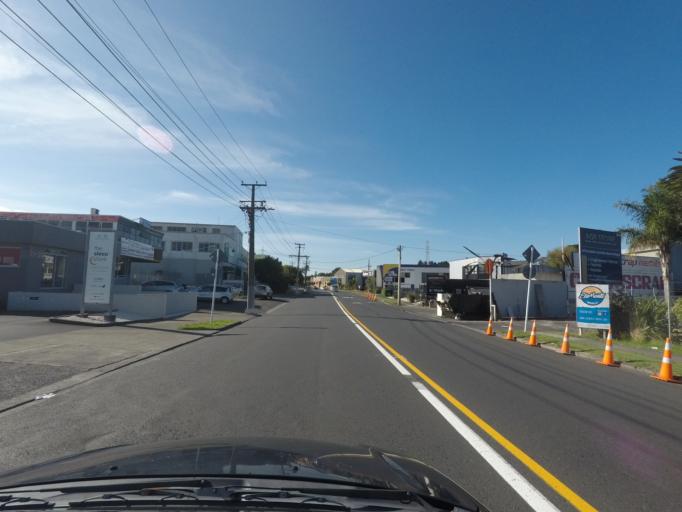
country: NZ
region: Auckland
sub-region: Auckland
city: Waitakere
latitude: -36.9073
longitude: 174.6906
